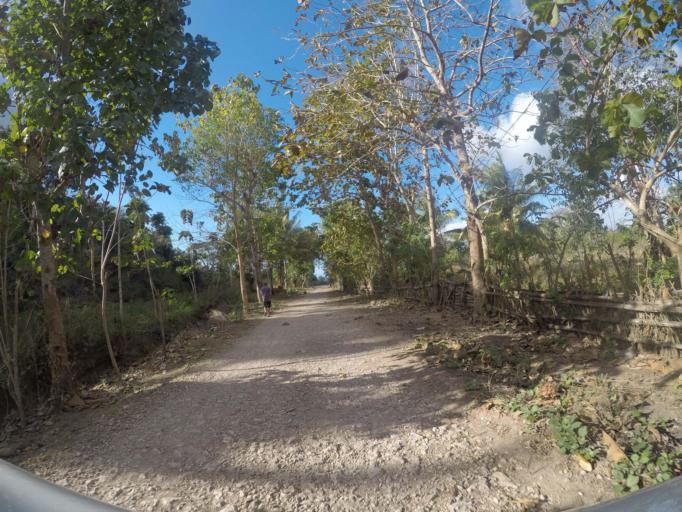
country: TL
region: Lautem
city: Lospalos
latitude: -8.4591
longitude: 126.8869
